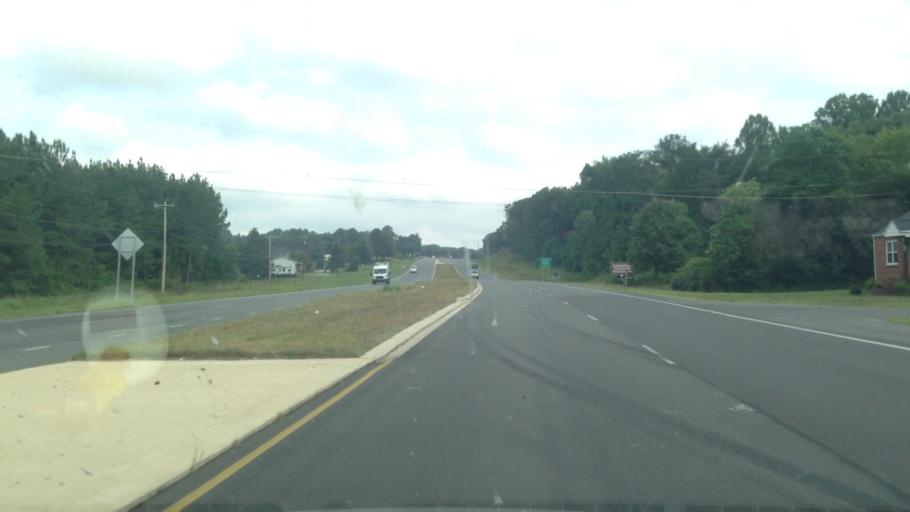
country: US
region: North Carolina
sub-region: Guilford County
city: Summerfield
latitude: 36.1770
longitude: -79.8829
